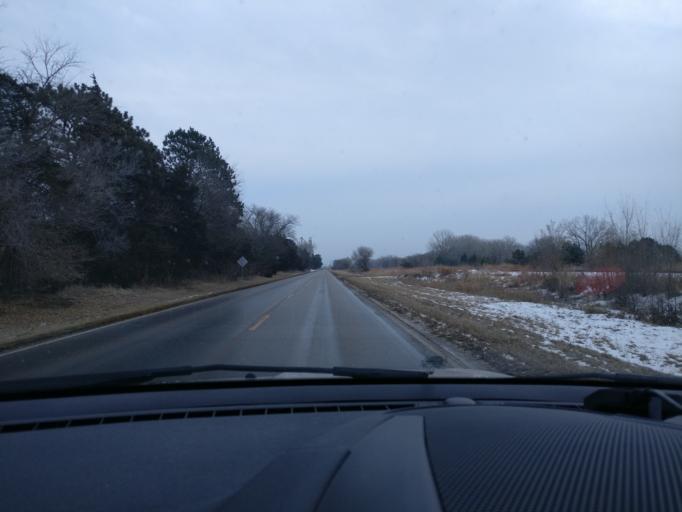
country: US
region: Nebraska
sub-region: Dodge County
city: Fremont
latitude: 41.4485
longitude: -96.5675
